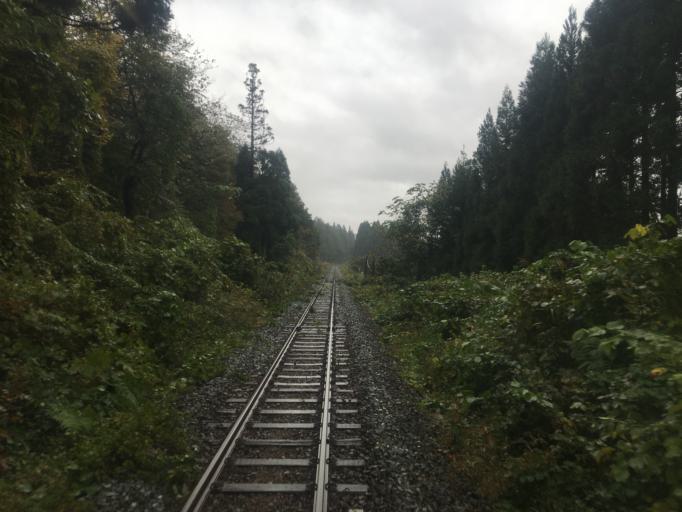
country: JP
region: Yamagata
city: Shinjo
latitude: 38.7655
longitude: 140.4354
